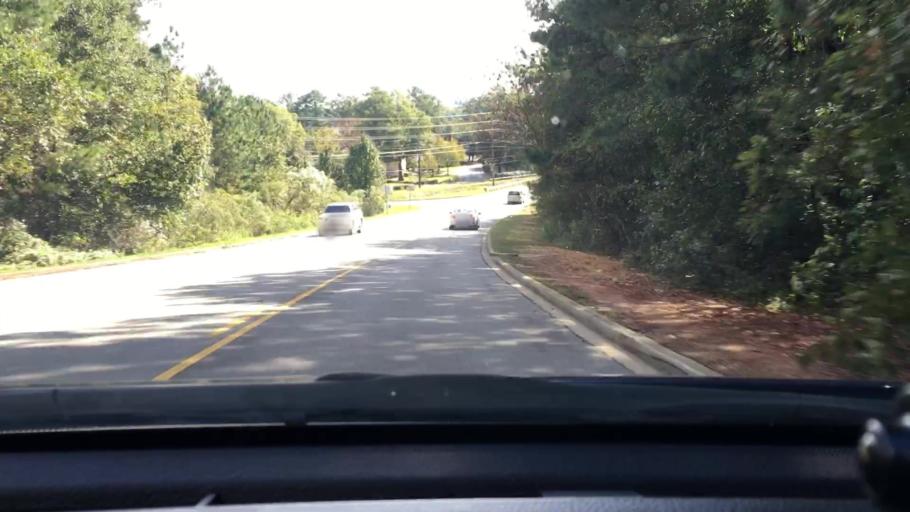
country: US
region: South Carolina
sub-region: Lexington County
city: Seven Oaks
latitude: 34.0701
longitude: -81.1487
